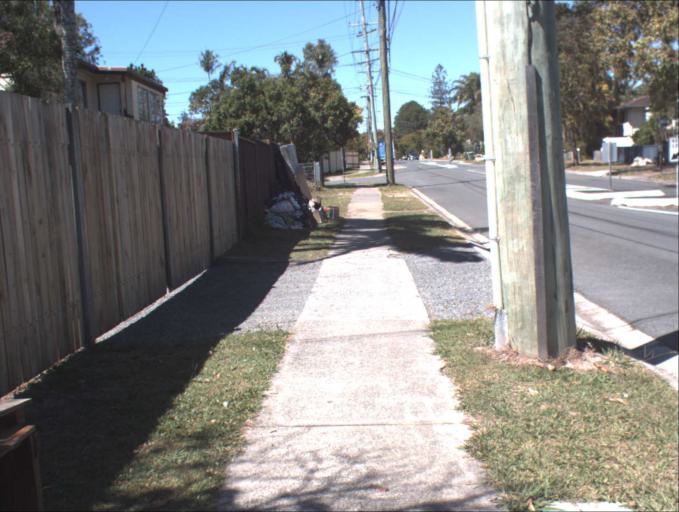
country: AU
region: Queensland
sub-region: Logan
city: Logan City
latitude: -27.6350
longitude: 153.1255
